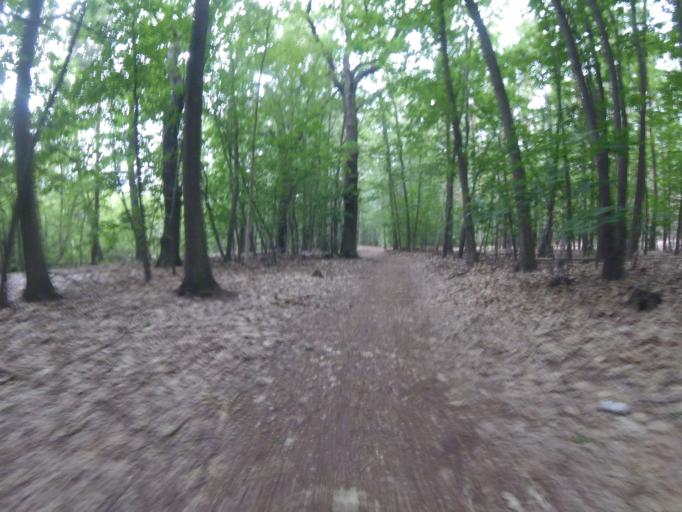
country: DE
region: Brandenburg
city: Bestensee
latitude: 52.2388
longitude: 13.6556
